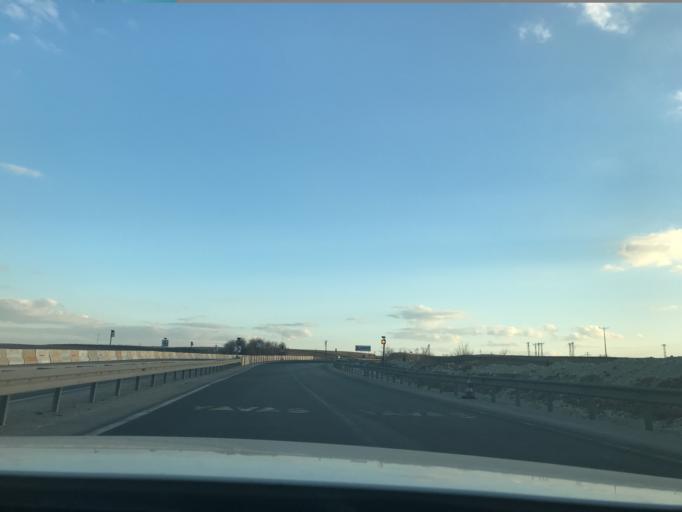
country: TR
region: Ankara
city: Ikizce
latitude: 39.5580
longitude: 32.8574
